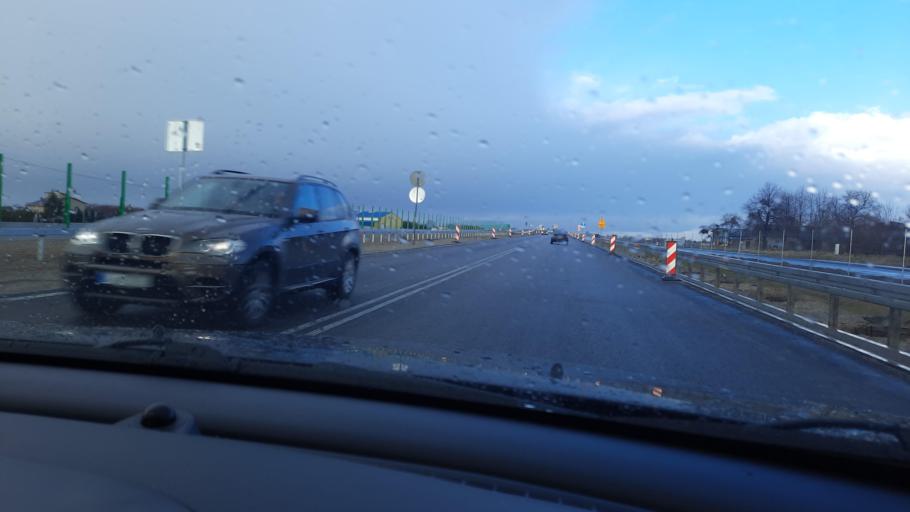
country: PL
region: Kujawsko-Pomorskie
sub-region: Powiat swiecki
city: Swiecie
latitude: 53.4256
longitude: 18.5098
